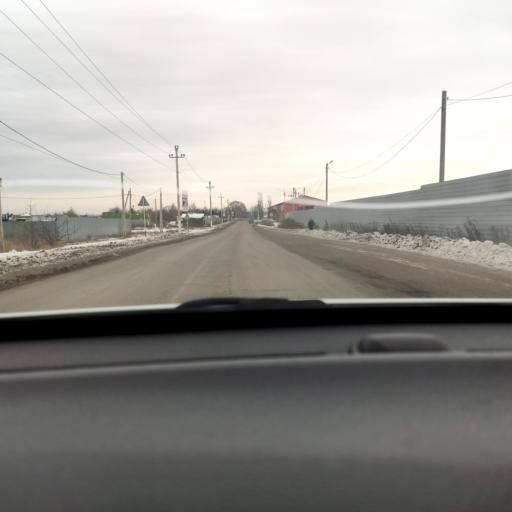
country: RU
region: Voronezj
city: Novaya Usman'
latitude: 51.6688
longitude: 39.3345
